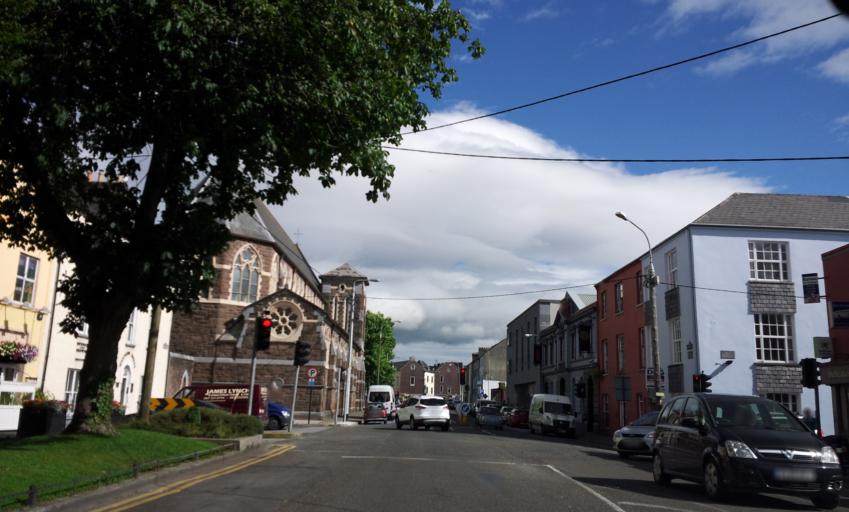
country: IE
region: Munster
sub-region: Ciarrai
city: Tralee
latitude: 52.2673
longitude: -9.7097
